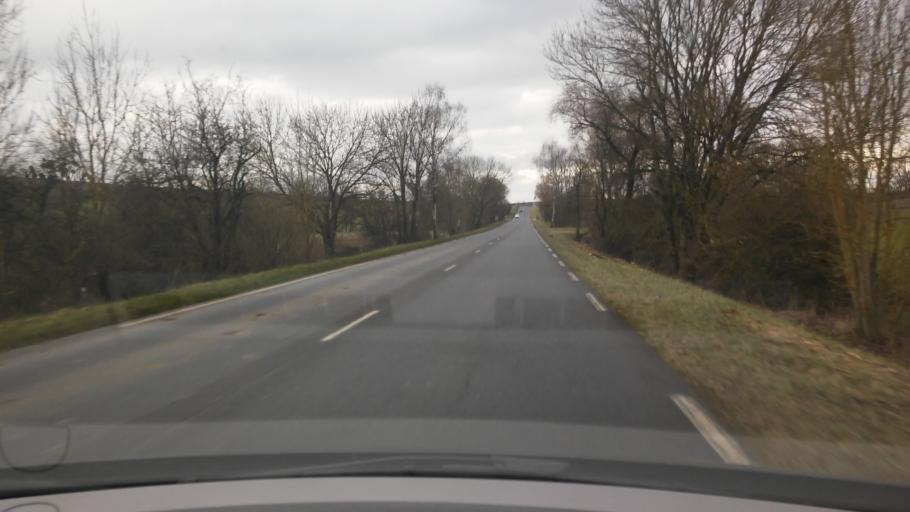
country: FR
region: Lorraine
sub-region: Departement de la Moselle
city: Courcelles-Chaussy
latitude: 49.0997
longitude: 6.4822
